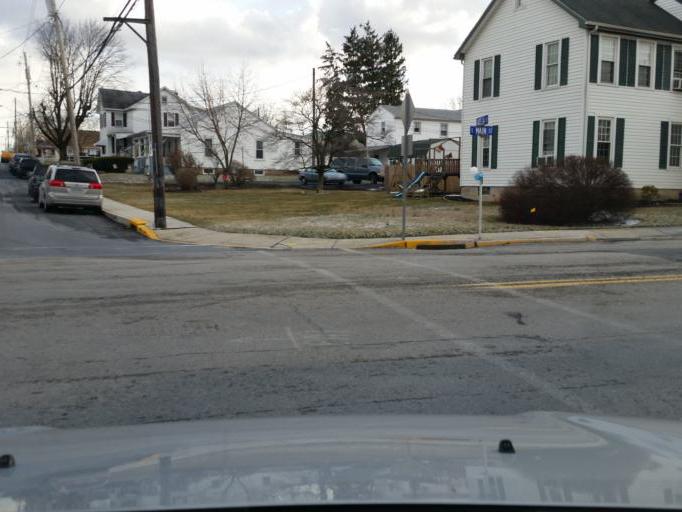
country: US
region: Pennsylvania
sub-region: Dauphin County
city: Middletown
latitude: 40.2011
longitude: -76.7212
